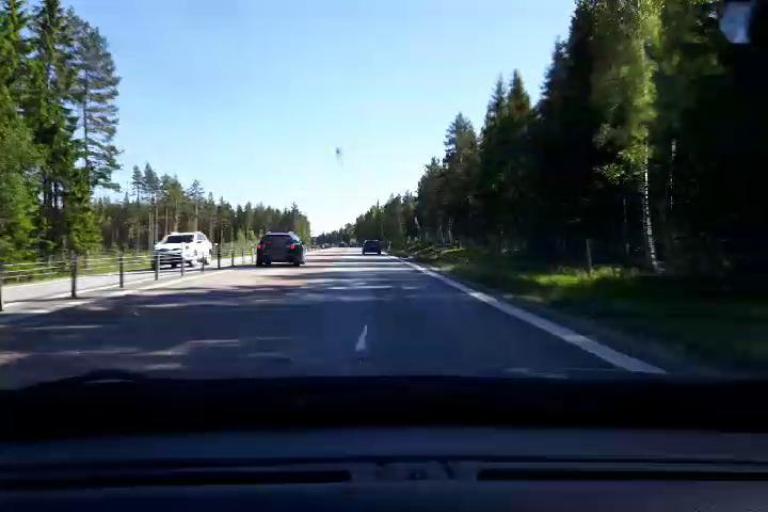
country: SE
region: Gaevleborg
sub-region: Gavle Kommun
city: Norrsundet
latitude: 60.8797
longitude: 17.0461
